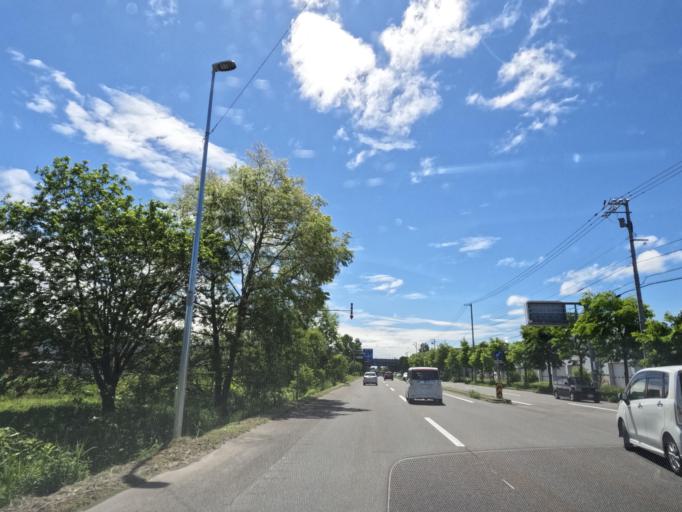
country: JP
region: Hokkaido
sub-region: Asahikawa-shi
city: Asahikawa
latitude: 43.7289
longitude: 142.3666
